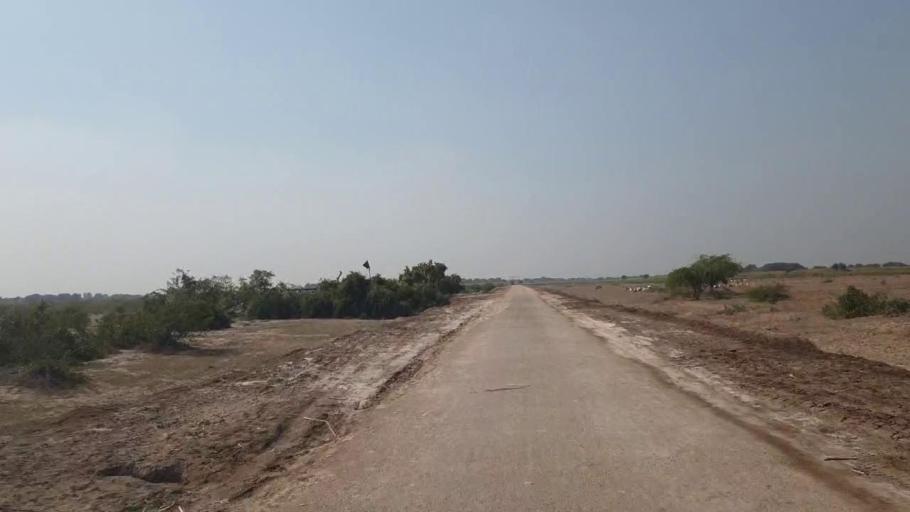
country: PK
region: Sindh
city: Chambar
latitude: 25.3812
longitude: 68.8868
